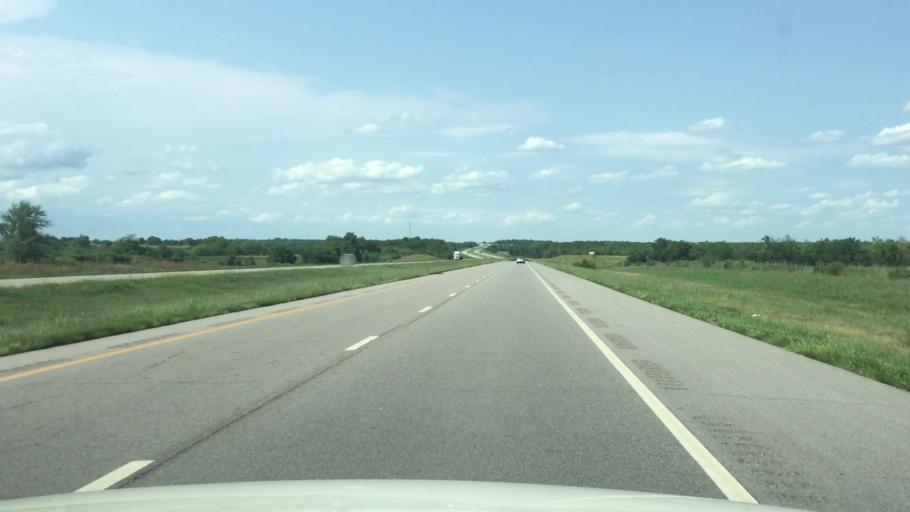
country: US
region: Kansas
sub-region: Linn County
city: La Cygne
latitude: 38.4416
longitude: -94.6863
